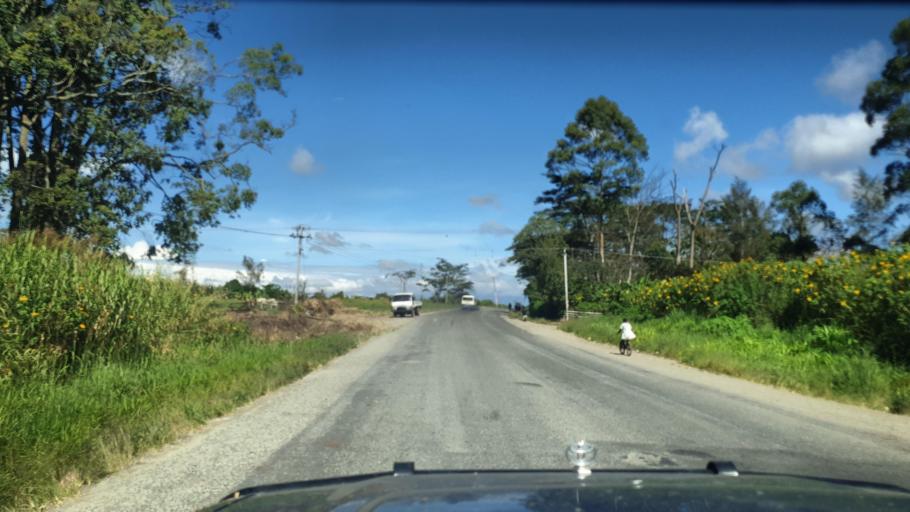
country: PG
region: Western Highlands
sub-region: Hagen
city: Mount Hagen
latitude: -5.8388
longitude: 144.3241
